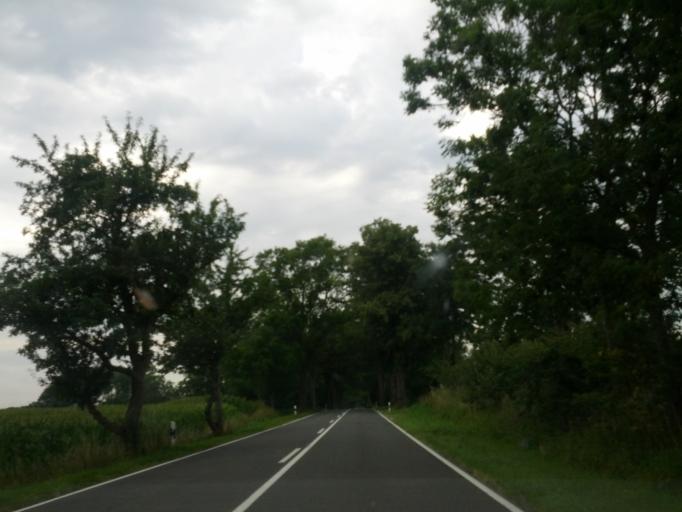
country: DE
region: Mecklenburg-Vorpommern
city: Satow-Oberhagen
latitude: 54.0043
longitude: 11.8277
